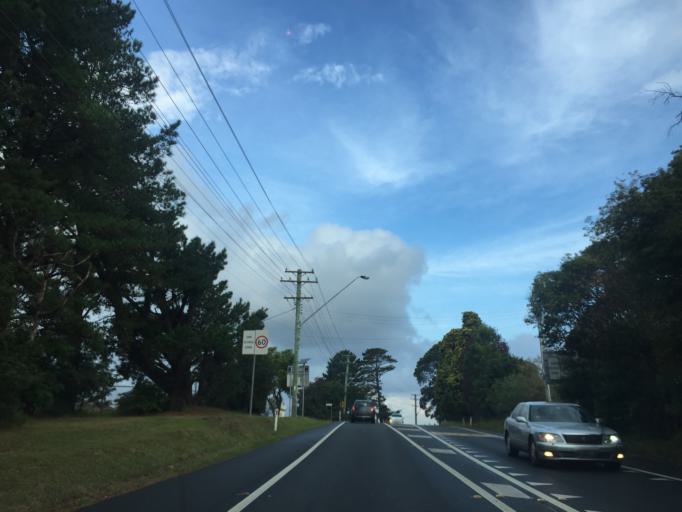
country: AU
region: New South Wales
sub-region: The Hills Shire
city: Glenhaven
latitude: -33.6910
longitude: 151.0317
